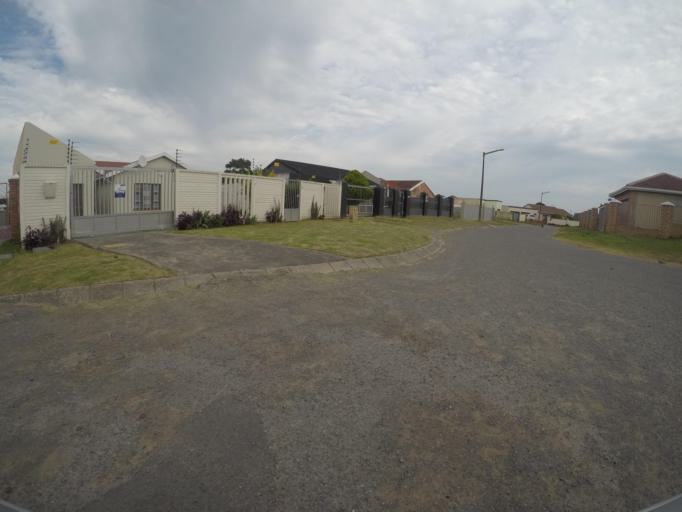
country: ZA
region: Eastern Cape
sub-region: Buffalo City Metropolitan Municipality
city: East London
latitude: -32.9774
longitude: 27.8583
